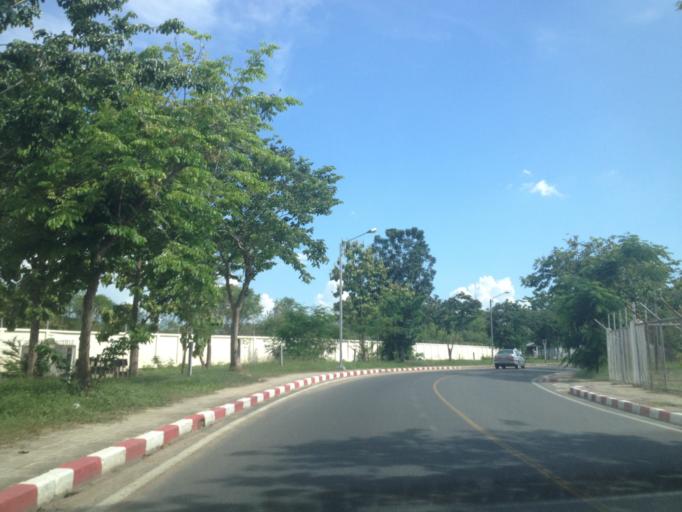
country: TH
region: Chiang Mai
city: Chiang Mai
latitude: 18.7638
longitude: 98.9690
